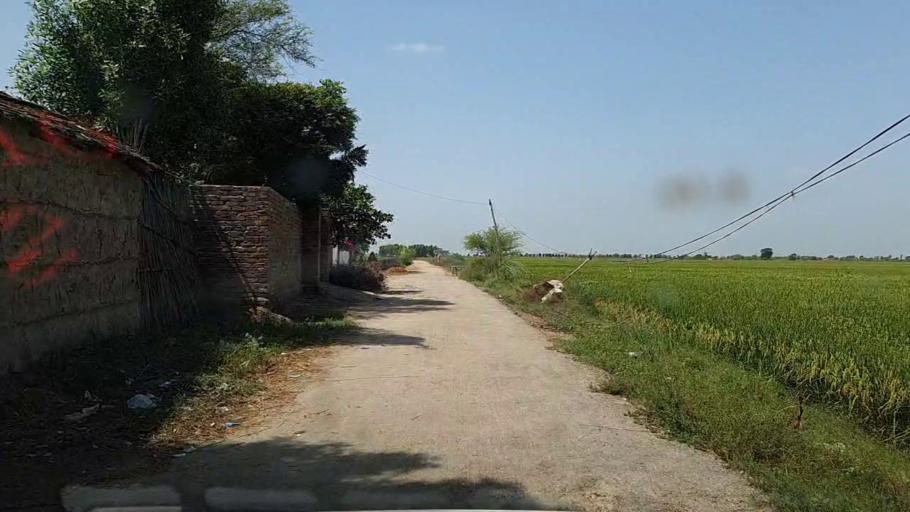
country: PK
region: Sindh
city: Kario
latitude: 24.6287
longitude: 68.5319
